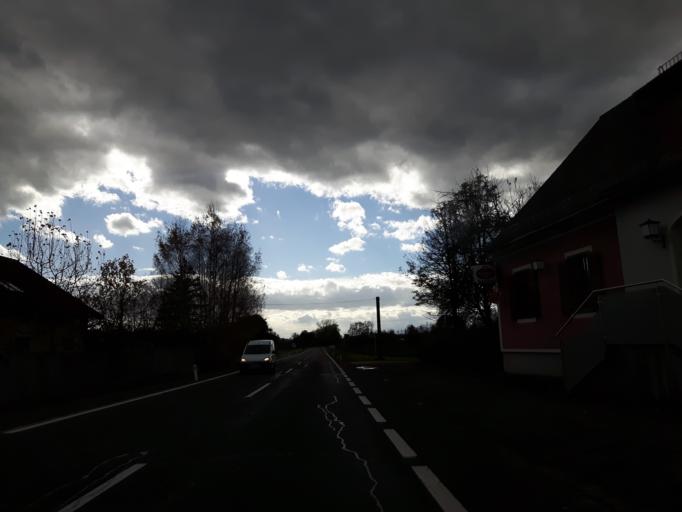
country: AT
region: Styria
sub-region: Politischer Bezirk Suedoststeiermark
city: Schwarzau im Schwarzautal
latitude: 46.8686
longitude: 15.6560
